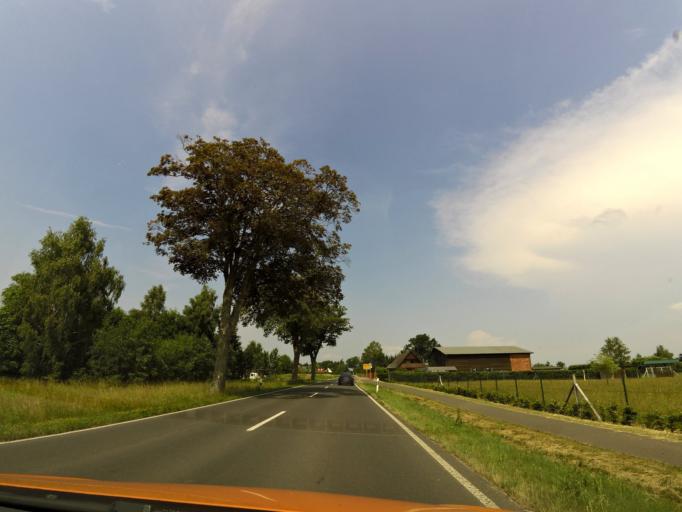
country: DE
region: Brandenburg
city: Pritzwalk
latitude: 53.1883
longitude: 12.1954
